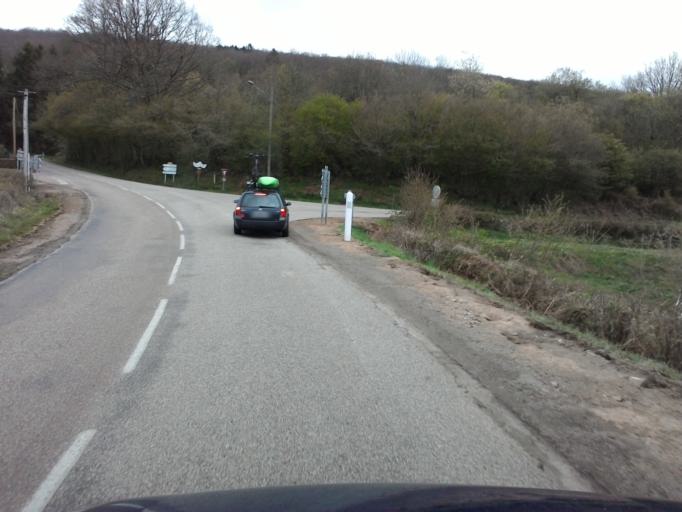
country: FR
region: Bourgogne
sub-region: Departement de la Cote-d'Or
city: Saulieu
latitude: 47.2455
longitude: 4.0714
